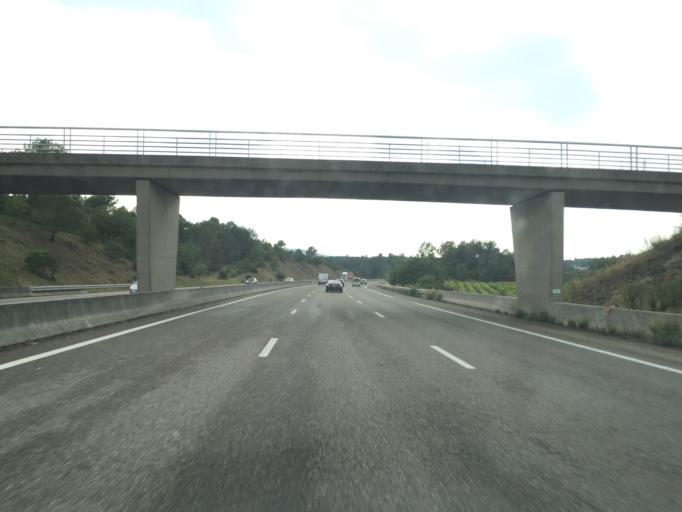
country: FR
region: Provence-Alpes-Cote d'Azur
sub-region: Departement du Var
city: Tourves
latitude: 43.4372
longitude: 5.9124
